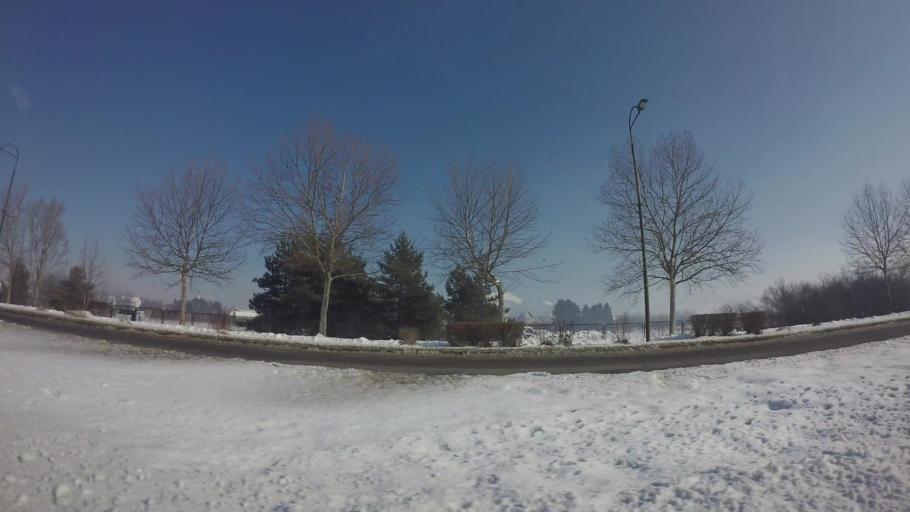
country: BA
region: Federation of Bosnia and Herzegovina
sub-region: Kanton Sarajevo
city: Sarajevo
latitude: 43.8074
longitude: 18.3109
